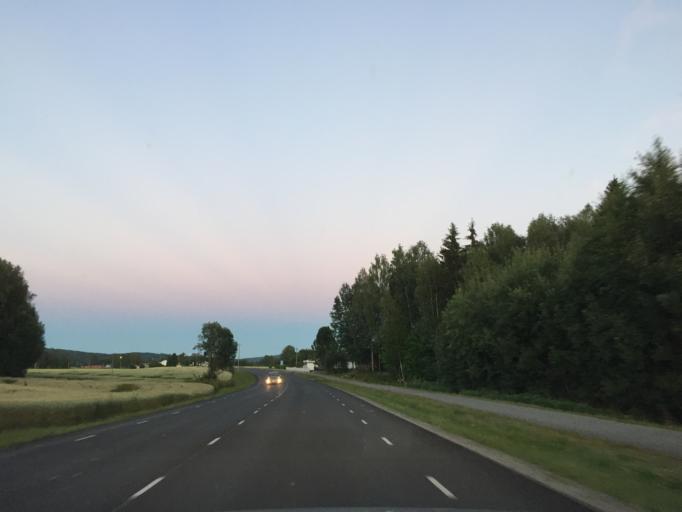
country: NO
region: Hedmark
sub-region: Kongsvinger
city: Spetalen
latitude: 60.2345
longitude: 11.8035
